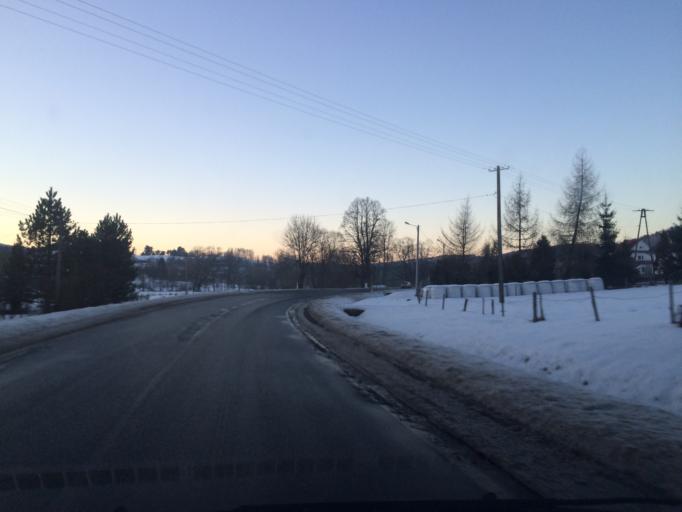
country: PL
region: Subcarpathian Voivodeship
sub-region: Powiat bieszczadzki
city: Czarna
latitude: 49.3732
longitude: 22.6471
